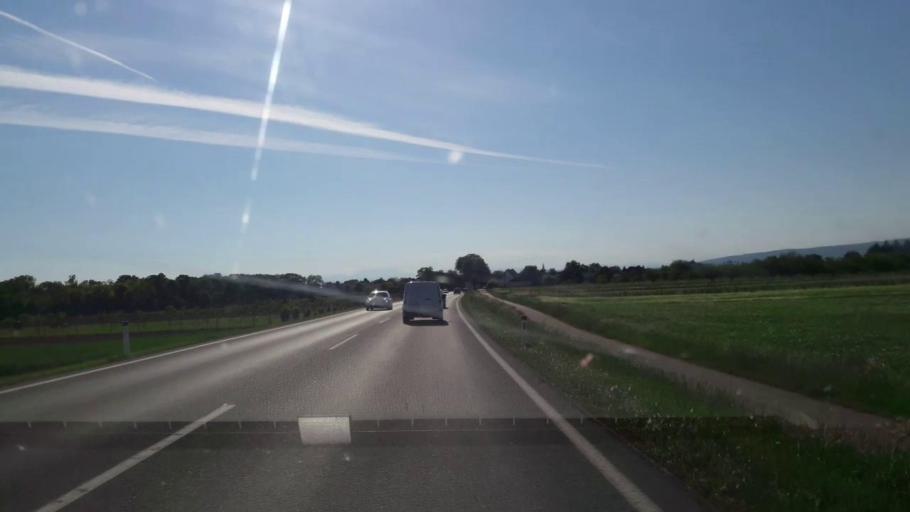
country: AT
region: Burgenland
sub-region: Eisenstadt-Umgebung
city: Sankt Margarethen im Burgenland
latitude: 47.8012
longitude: 16.6260
